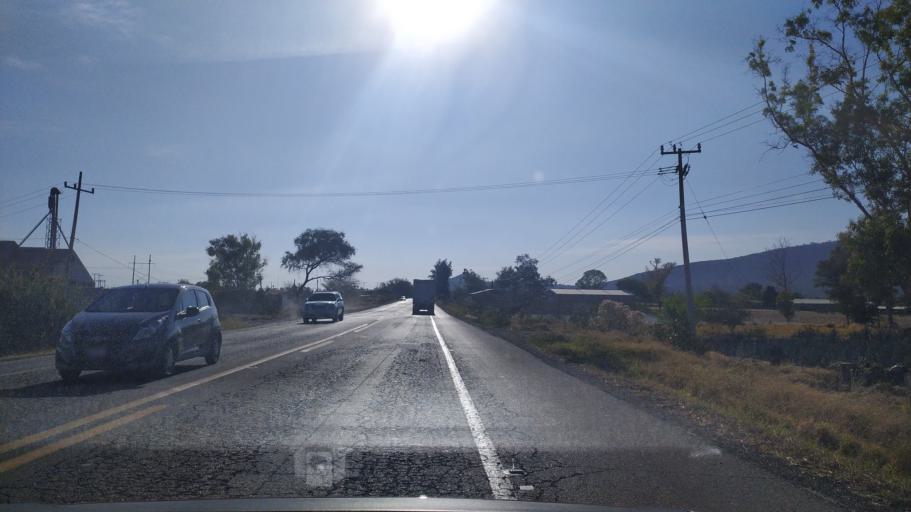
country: MX
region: Jalisco
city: Jamay
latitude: 20.2940
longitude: -102.6645
